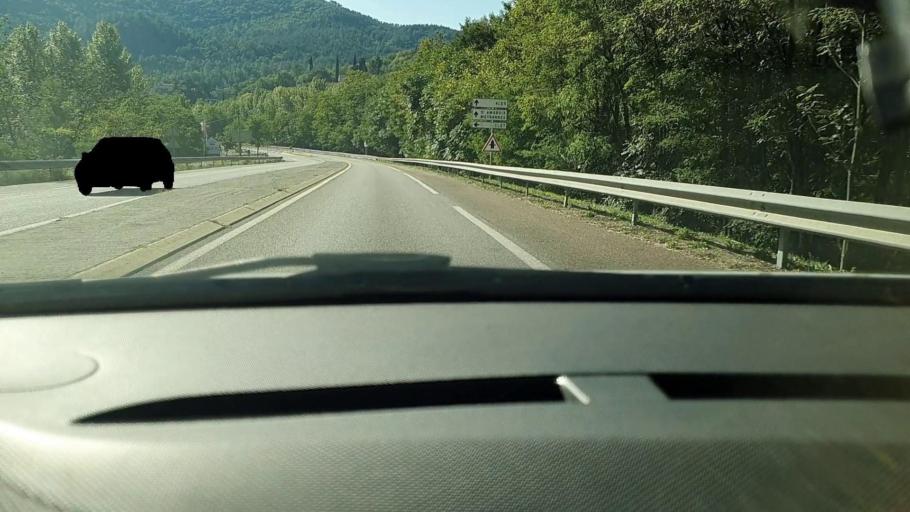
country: FR
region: Languedoc-Roussillon
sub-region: Departement du Gard
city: Molieres-sur-Ceze
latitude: 44.2661
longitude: 4.1535
